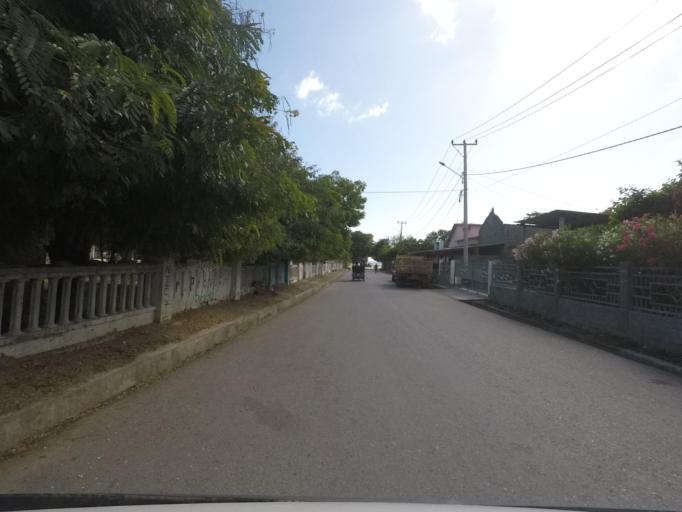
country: TL
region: Manatuto
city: Manatuto
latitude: -8.5111
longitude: 126.0137
